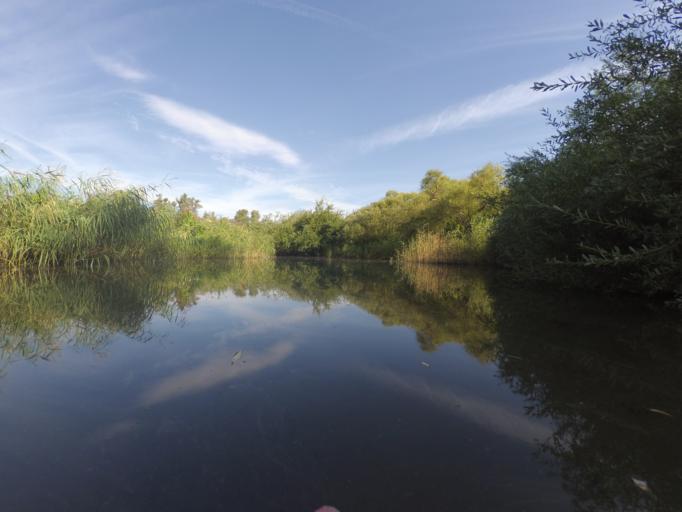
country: NL
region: North Brabant
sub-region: Gemeente Made en Drimmelen
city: Drimmelen
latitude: 51.7319
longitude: 4.8316
